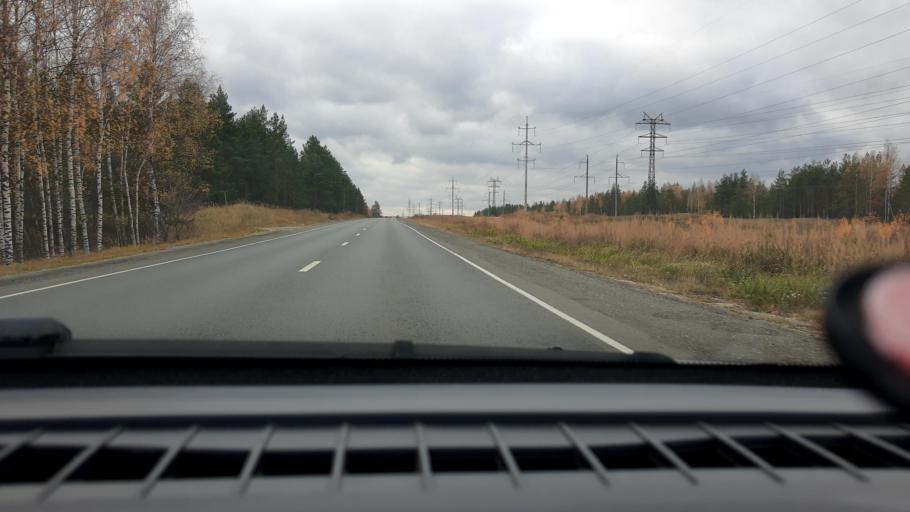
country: RU
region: Nizjnij Novgorod
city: Lukino
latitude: 56.3492
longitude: 43.5866
